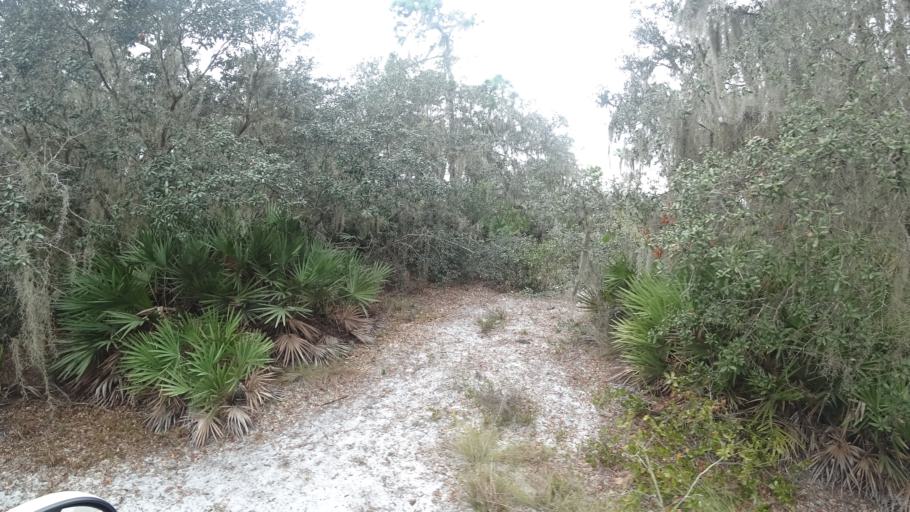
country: US
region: Florida
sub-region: Hillsborough County
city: Wimauma
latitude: 27.5612
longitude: -82.1372
